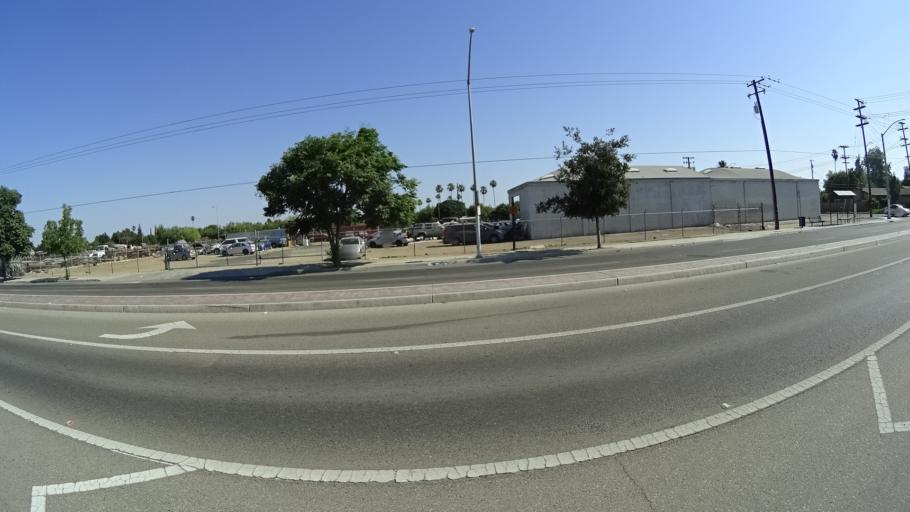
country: US
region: California
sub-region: Fresno County
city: West Park
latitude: 36.7213
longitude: -119.8184
